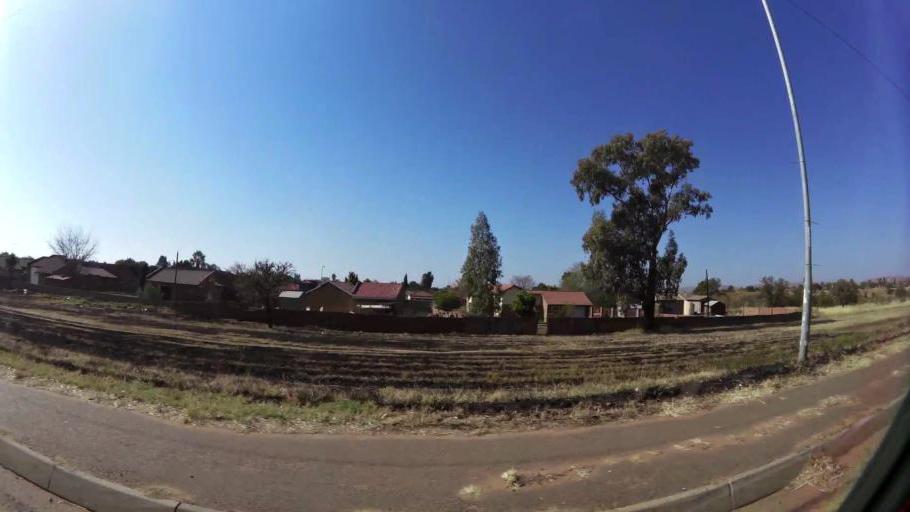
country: ZA
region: North-West
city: Ga-Rankuwa
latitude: -25.6535
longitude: 28.1022
